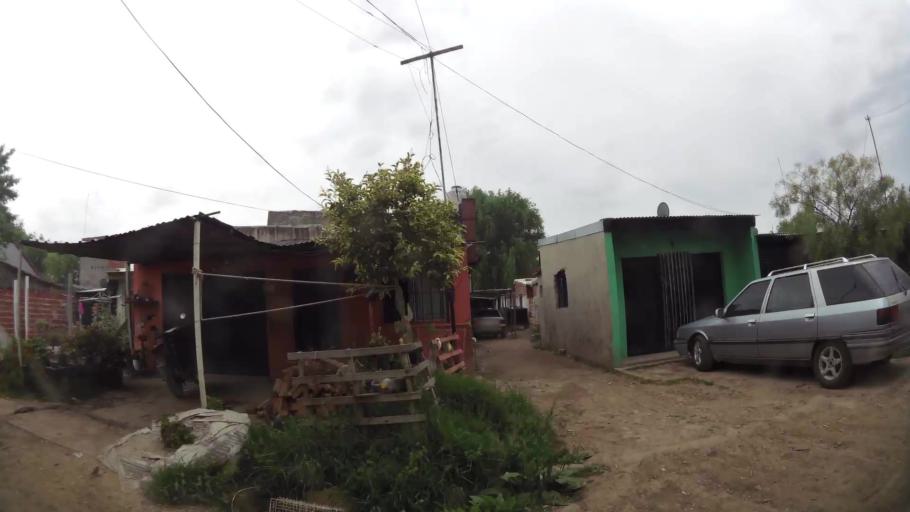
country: AR
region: Buenos Aires
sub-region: Partido de Zarate
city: Zarate
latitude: -34.1163
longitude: -59.0413
